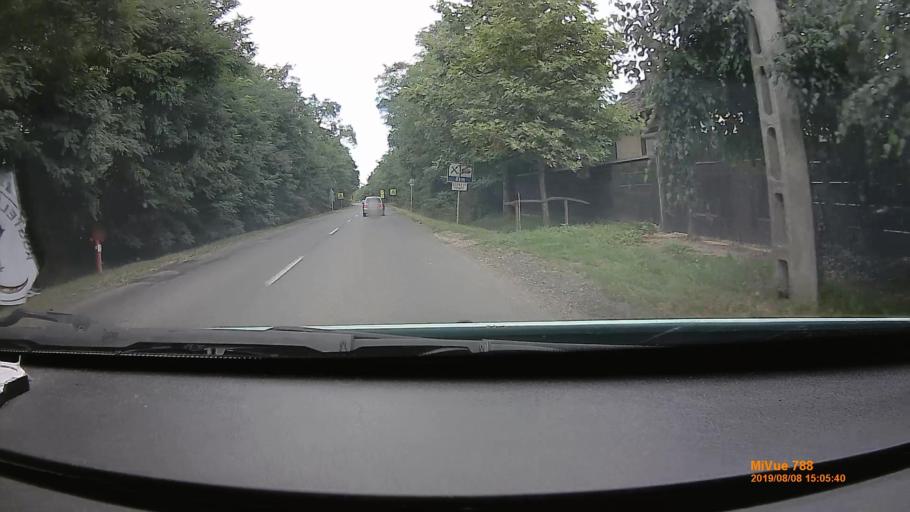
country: HU
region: Szabolcs-Szatmar-Bereg
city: Kocsord
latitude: 47.9435
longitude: 22.4276
